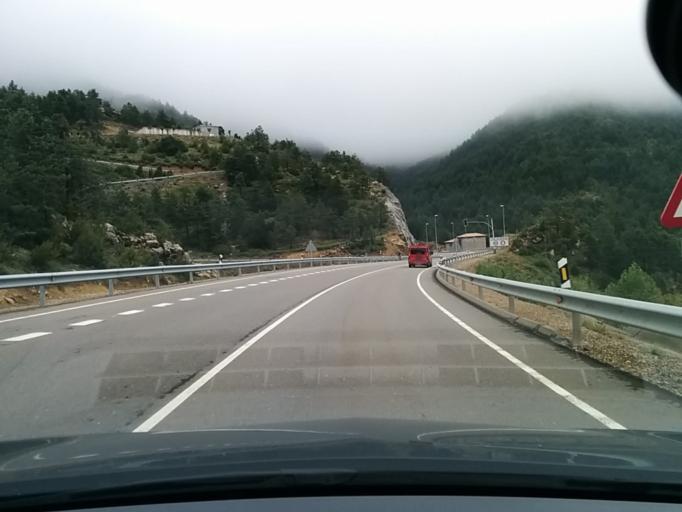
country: ES
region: Aragon
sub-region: Provincia de Huesca
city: Fiscal
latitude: 42.4684
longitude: -0.1932
